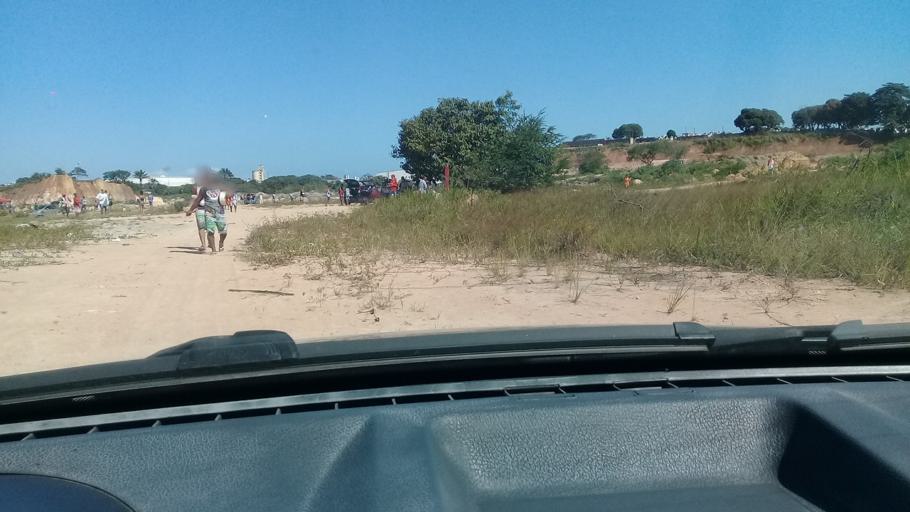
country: BR
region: Pernambuco
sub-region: Jaboatao Dos Guararapes
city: Jaboatao
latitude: -8.1479
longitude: -34.9494
